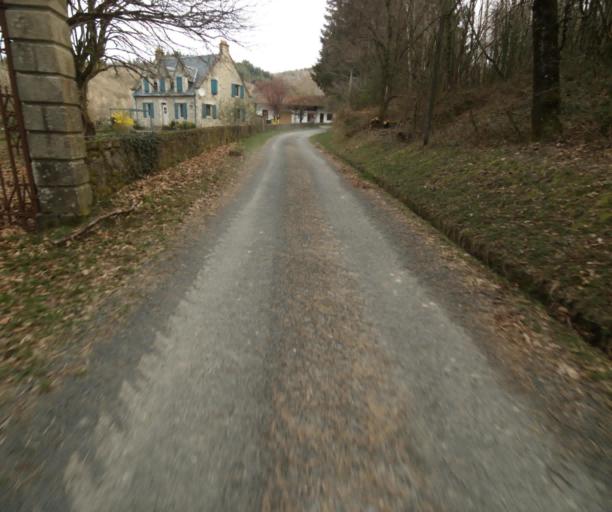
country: FR
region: Limousin
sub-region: Departement de la Correze
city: Treignac
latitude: 45.4718
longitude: 1.8310
